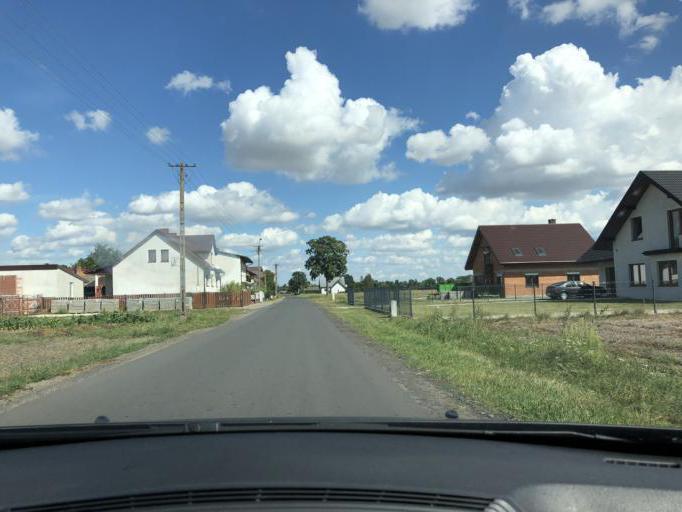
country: PL
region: Lodz Voivodeship
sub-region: Powiat wieruszowski
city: Czastary
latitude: 51.2354
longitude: 18.3566
